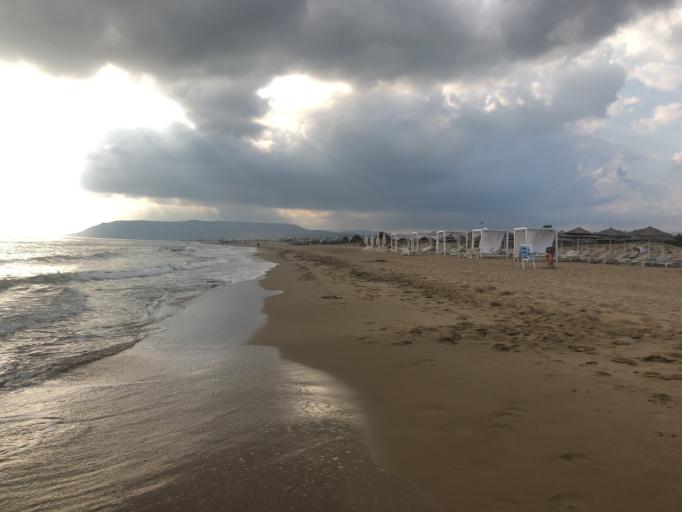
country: GR
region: Crete
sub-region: Nomos Chanias
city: Georgioupolis
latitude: 35.3562
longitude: 24.2816
